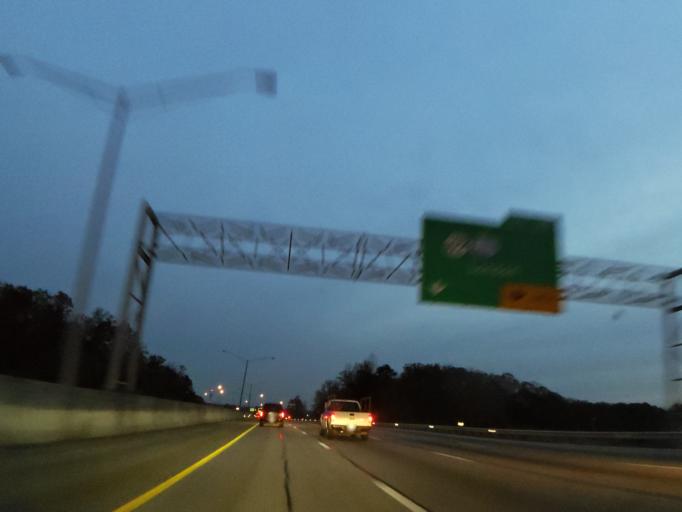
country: US
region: Kentucky
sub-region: Laurel County
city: London
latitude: 37.1196
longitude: -84.1058
